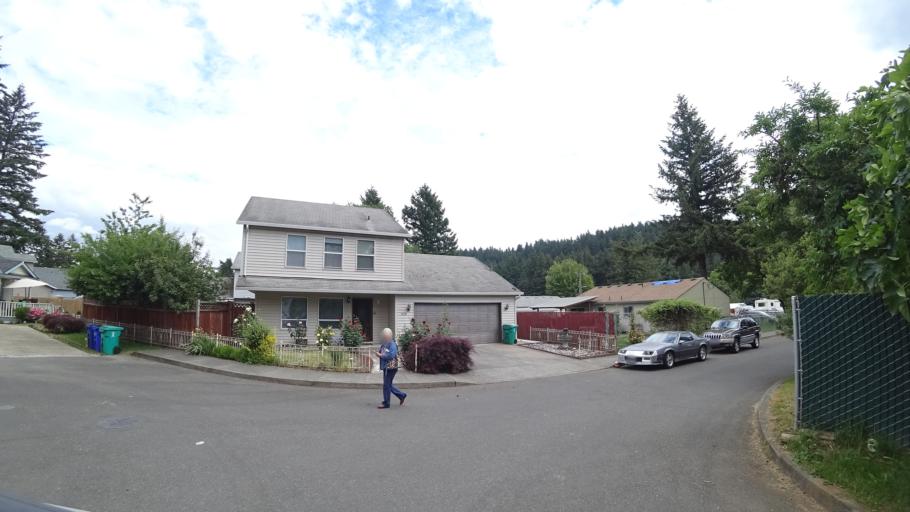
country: US
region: Oregon
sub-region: Clackamas County
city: Happy Valley
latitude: 45.4938
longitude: -122.5191
